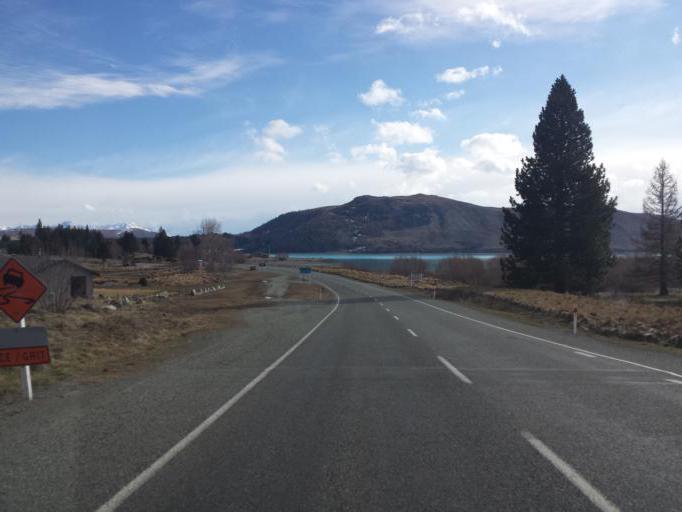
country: NZ
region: Canterbury
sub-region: Timaru District
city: Pleasant Point
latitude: -44.0084
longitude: 170.4950
